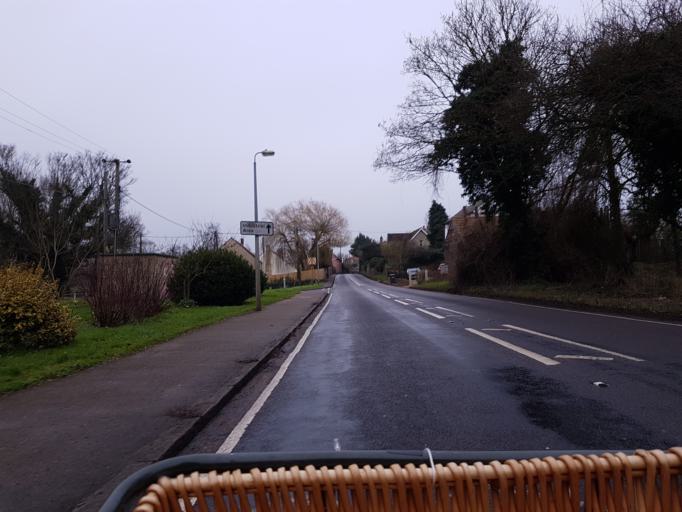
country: GB
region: England
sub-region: Cambridgeshire
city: Duxford
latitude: 52.0666
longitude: 0.1933
